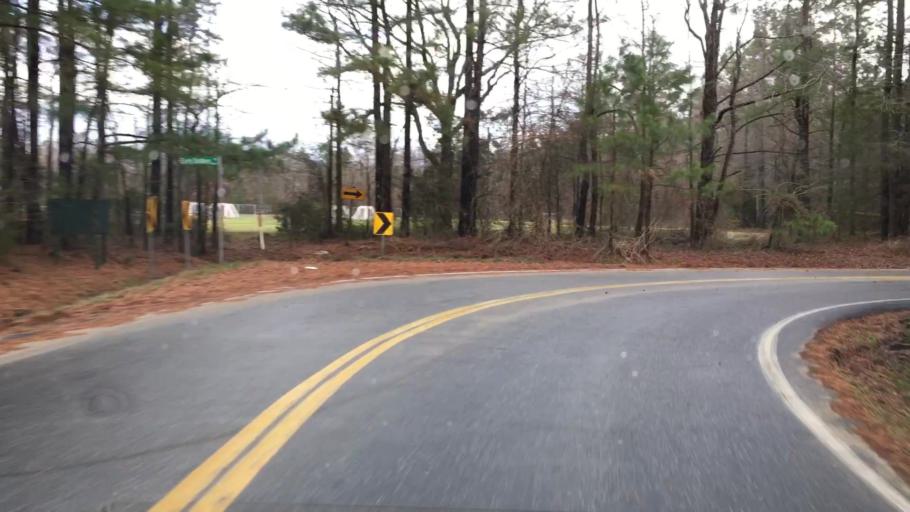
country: US
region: Virginia
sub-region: Chesterfield County
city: Bon Air
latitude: 37.5120
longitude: -77.5979
